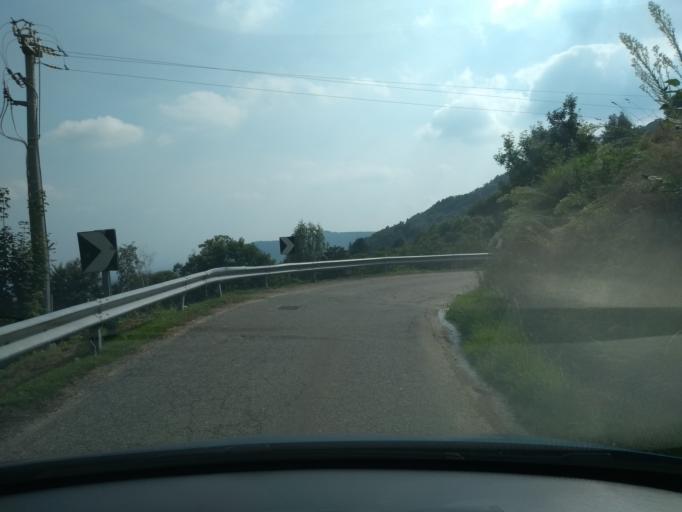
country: IT
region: Piedmont
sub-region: Provincia di Torino
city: Corio
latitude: 45.3281
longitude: 7.5180
